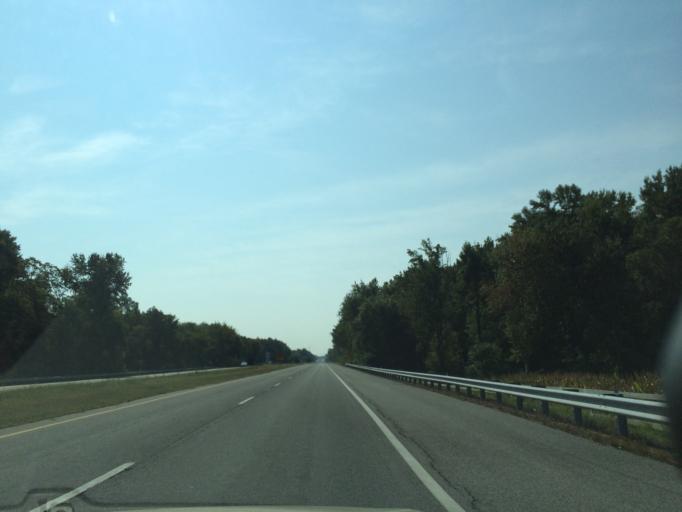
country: US
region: Maryland
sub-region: Charles County
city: La Plata
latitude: 38.4423
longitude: -76.9833
